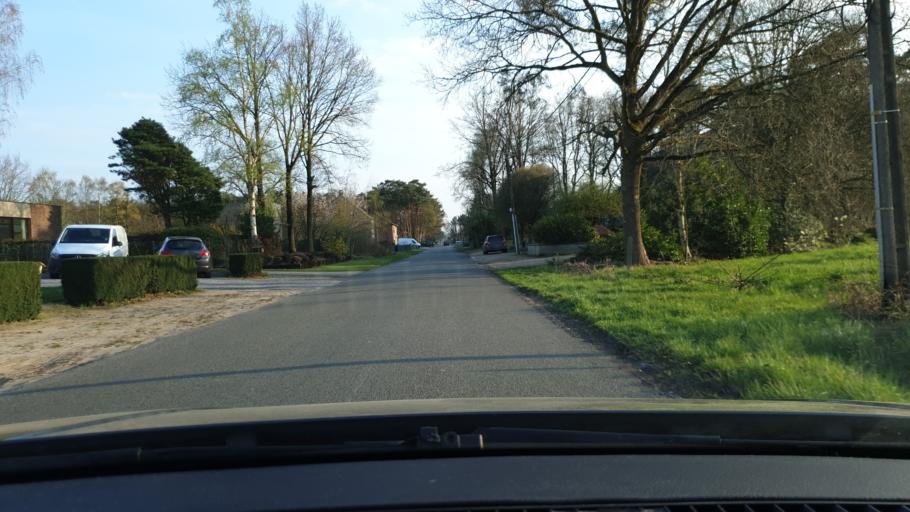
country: BE
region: Flanders
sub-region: Provincie Antwerpen
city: Geel
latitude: 51.1347
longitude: 5.0073
